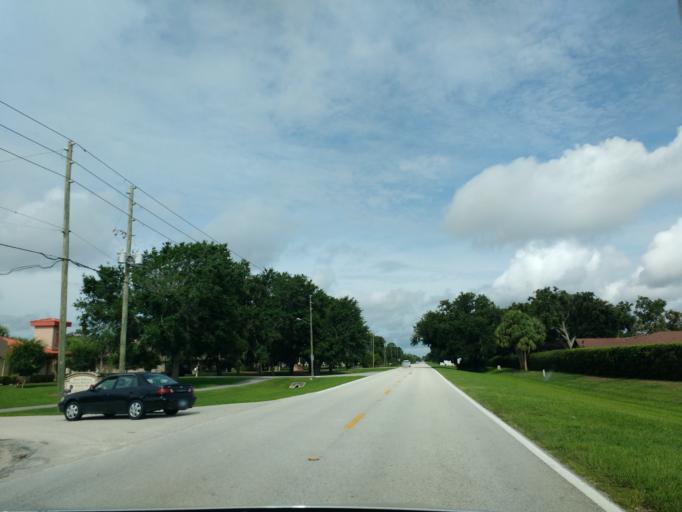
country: US
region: Florida
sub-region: Highlands County
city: Sebring
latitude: 27.4709
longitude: -81.4987
